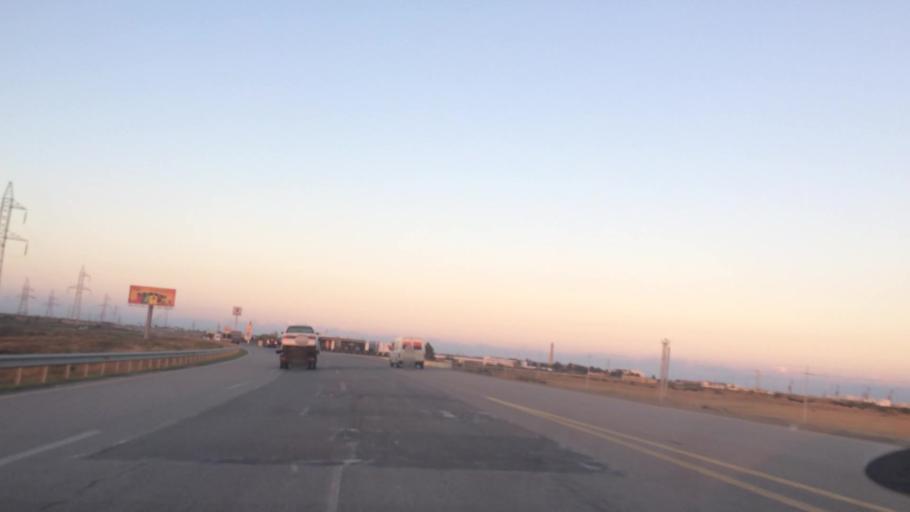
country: AZ
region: Baki
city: Qobustan
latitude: 39.9674
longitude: 49.4125
